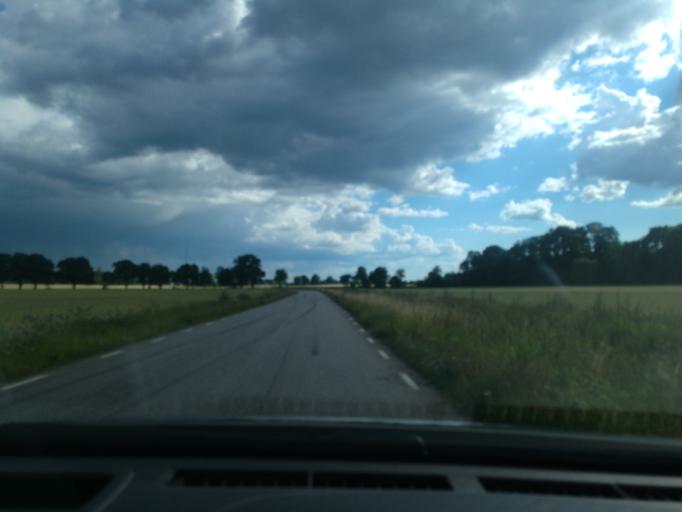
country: SE
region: Soedermanland
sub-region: Eskilstuna Kommun
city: Arla
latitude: 59.4456
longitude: 16.7213
